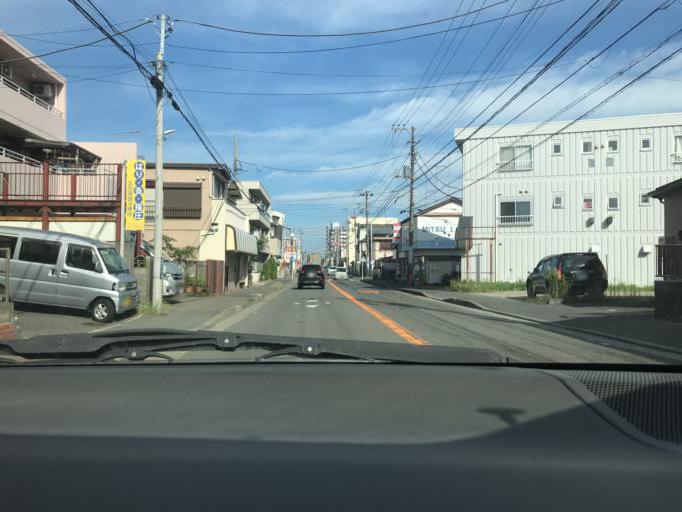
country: JP
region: Kanagawa
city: Fujisawa
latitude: 35.3417
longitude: 139.4575
